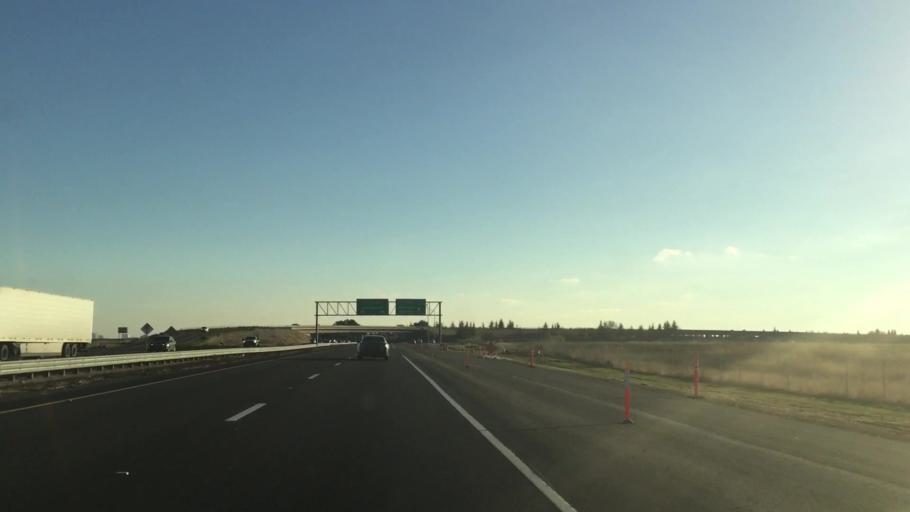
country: US
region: California
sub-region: Sacramento County
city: Elverta
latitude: 38.6753
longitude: -121.5402
